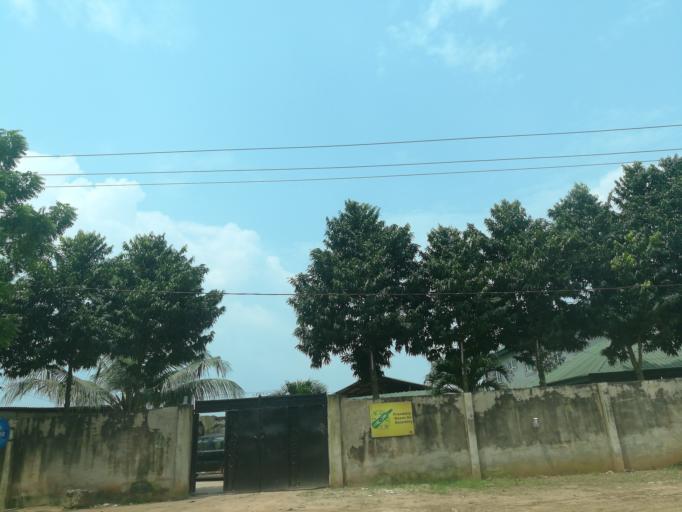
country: NG
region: Lagos
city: Ikorodu
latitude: 6.6074
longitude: 3.5939
